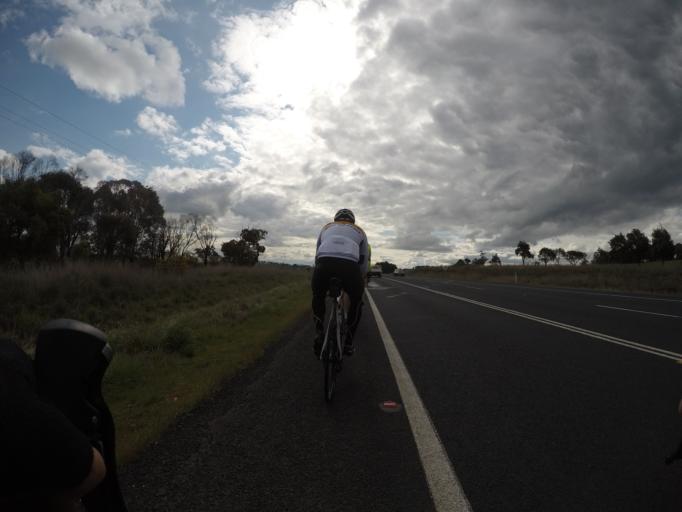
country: AU
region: New South Wales
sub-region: Blayney
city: Millthorpe
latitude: -33.3927
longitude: 149.2283
